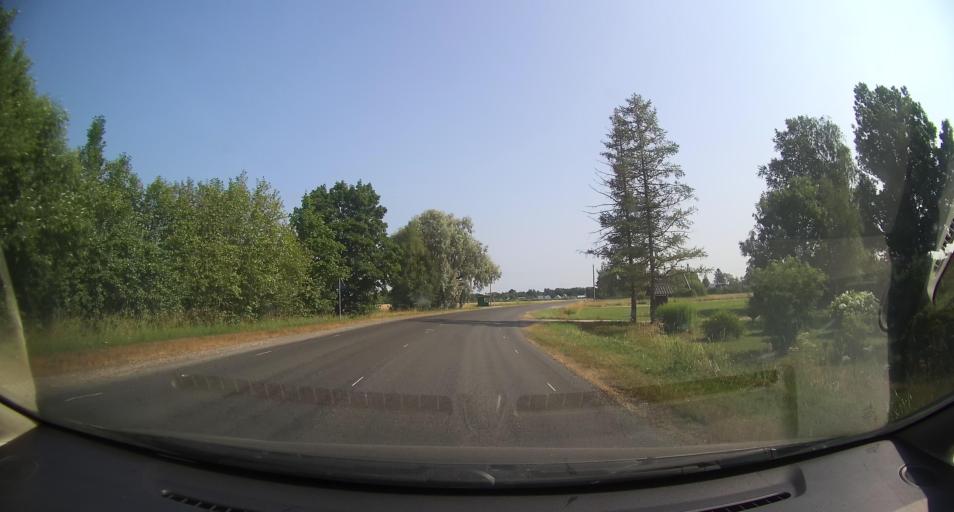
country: EE
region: Paernumaa
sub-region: Audru vald
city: Audru
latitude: 58.4656
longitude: 24.3133
